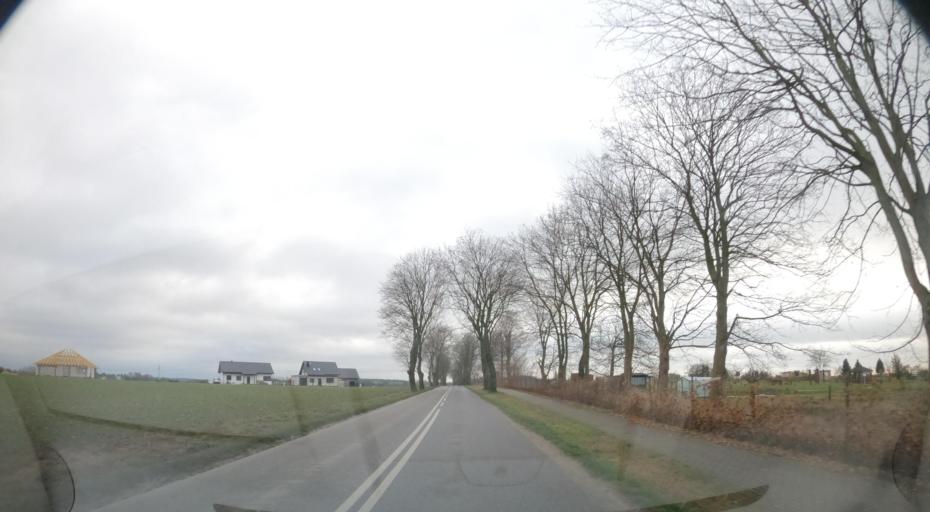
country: PL
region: Greater Poland Voivodeship
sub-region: Powiat pilski
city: Lobzenica
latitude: 53.2556
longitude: 17.2644
